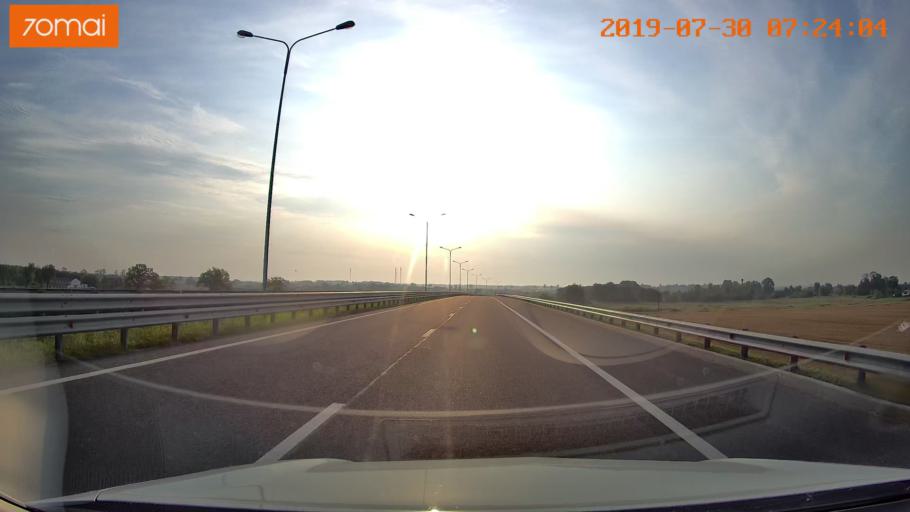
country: RU
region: Kaliningrad
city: Bol'shoe Isakovo
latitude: 54.6932
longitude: 20.8013
